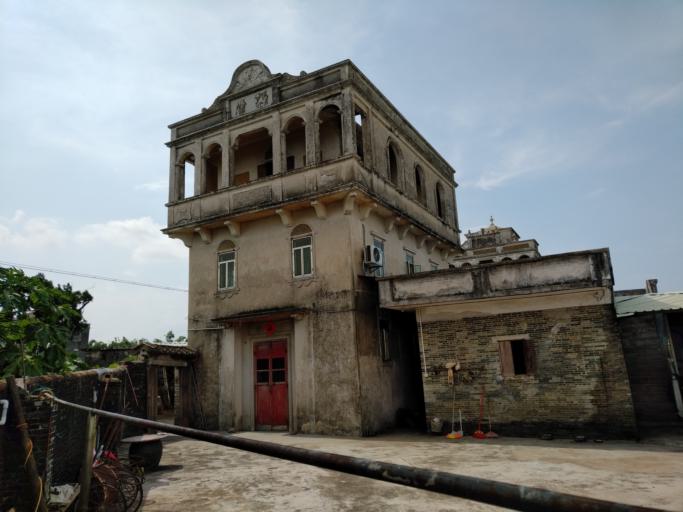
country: CN
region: Guangdong
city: Doushan
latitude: 22.0355
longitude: 112.8060
